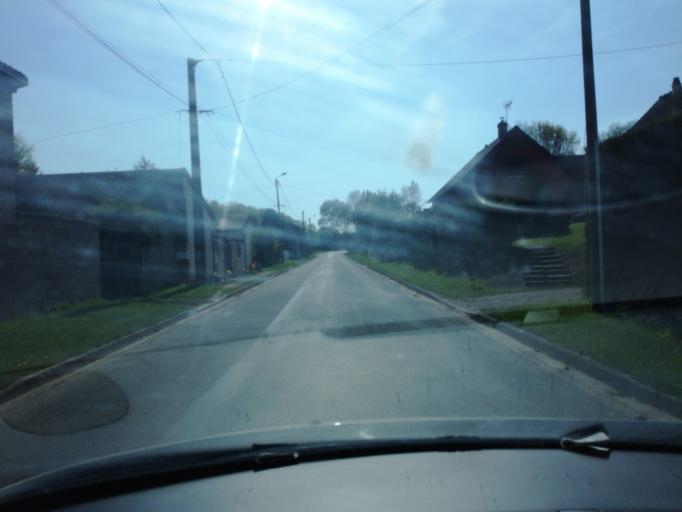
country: FR
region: Picardie
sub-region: Departement de la Somme
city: Quevauvillers
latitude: 49.8339
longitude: 2.0531
